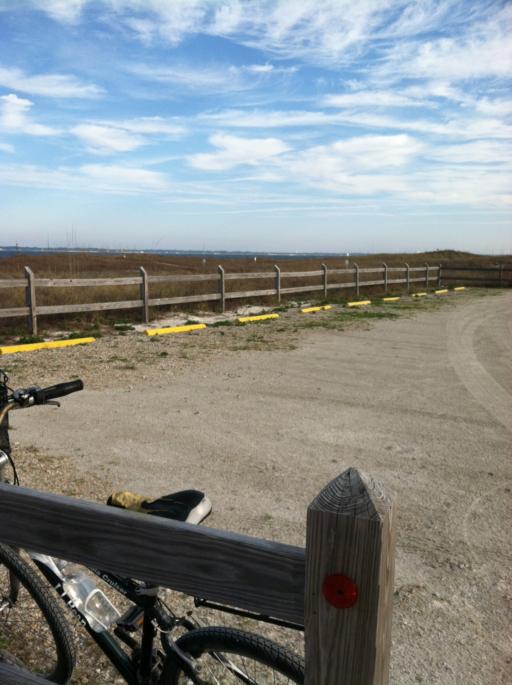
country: US
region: Florida
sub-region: Franklin County
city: Carrabelle
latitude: 29.7691
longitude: -84.6966
